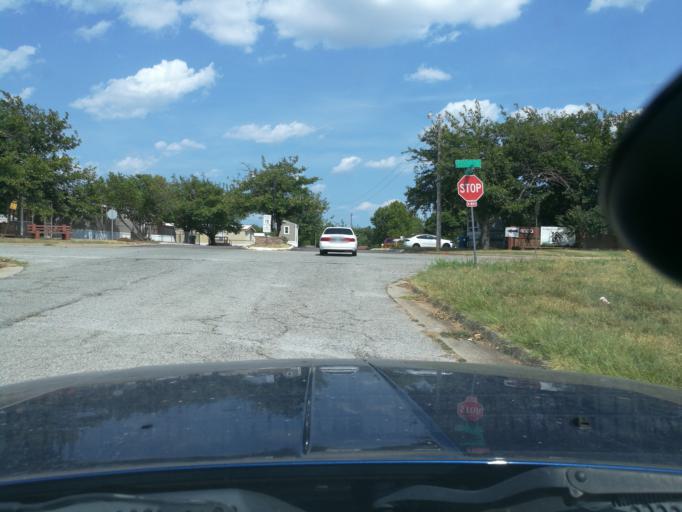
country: US
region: Oklahoma
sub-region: Oklahoma County
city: Del City
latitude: 35.4171
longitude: -97.4743
